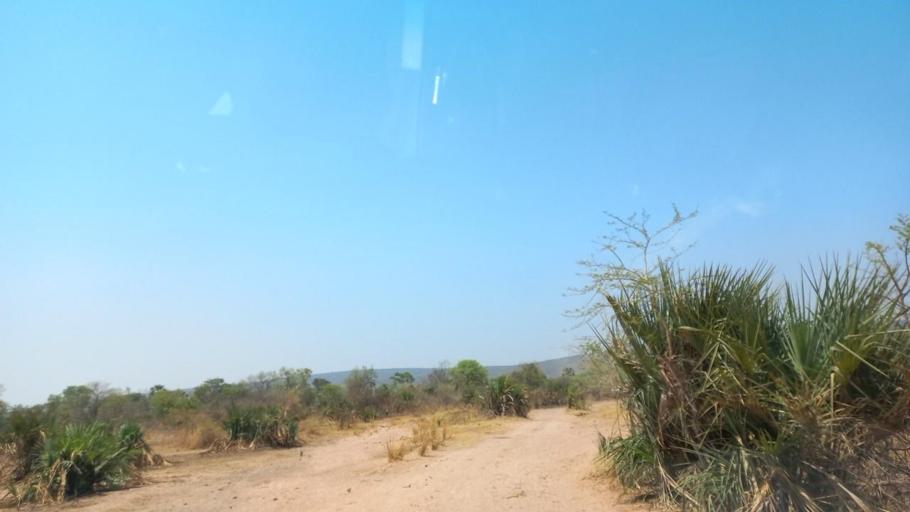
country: ZM
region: Lusaka
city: Luangwa
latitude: -15.1990
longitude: 30.1906
